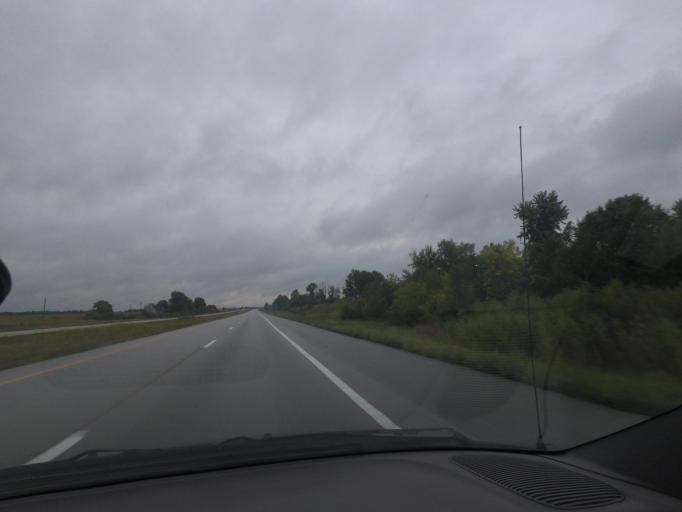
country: US
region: Missouri
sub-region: Marion County
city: Monroe City
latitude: 39.6644
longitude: -91.7308
